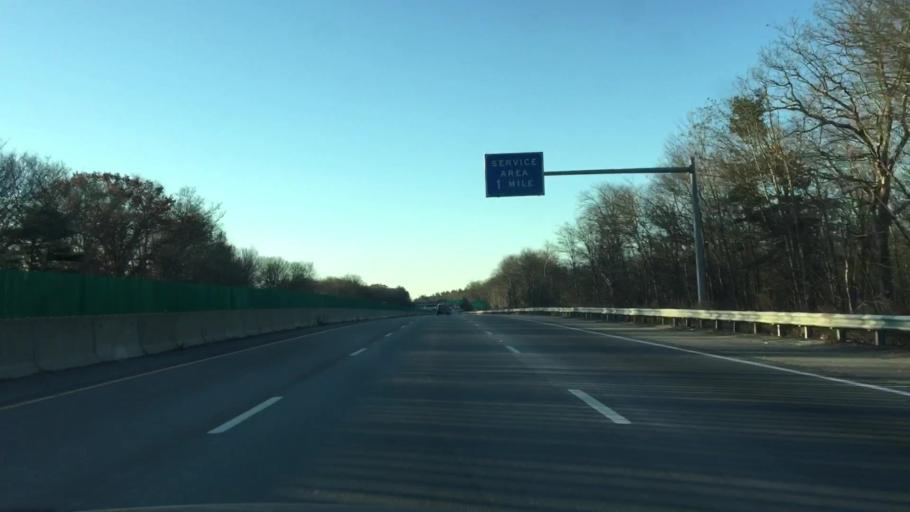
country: US
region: Massachusetts
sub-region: Plymouth County
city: West Bridgewater
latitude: 41.9756
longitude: -71.0262
